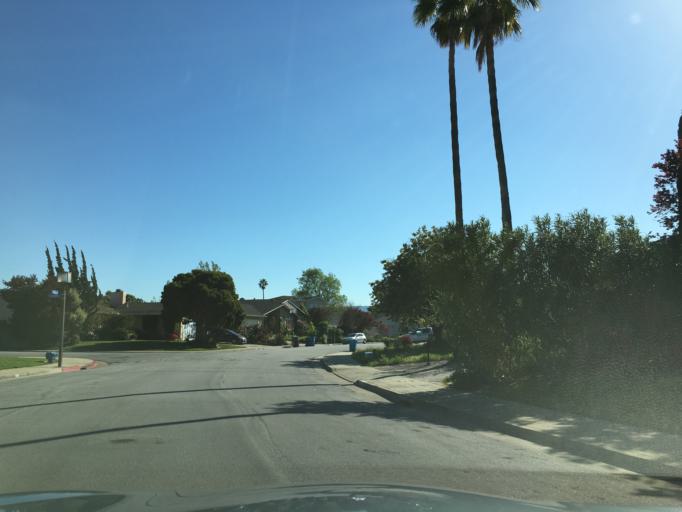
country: US
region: California
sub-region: San Mateo County
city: Redwood Shores
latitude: 37.5273
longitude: -122.2484
